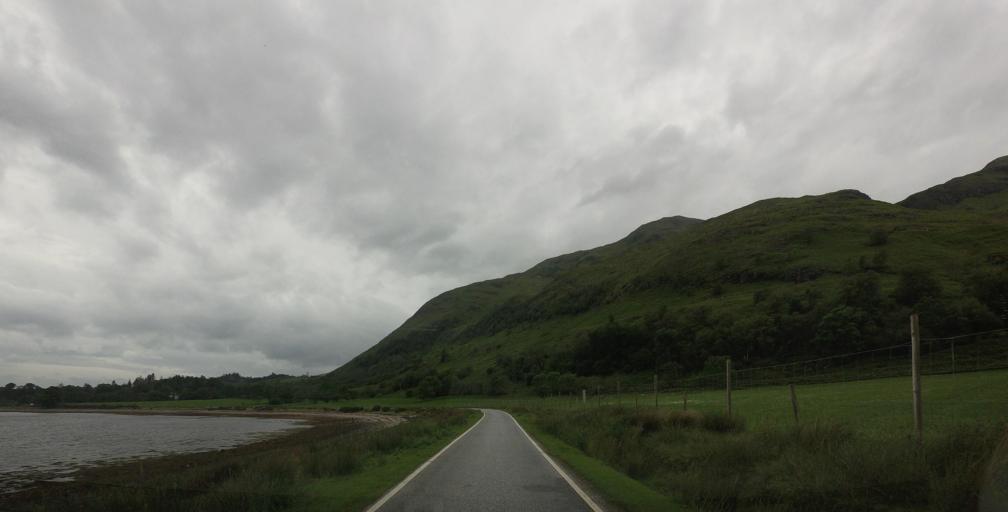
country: GB
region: Scotland
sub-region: Highland
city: Fort William
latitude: 56.7389
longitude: -5.2503
